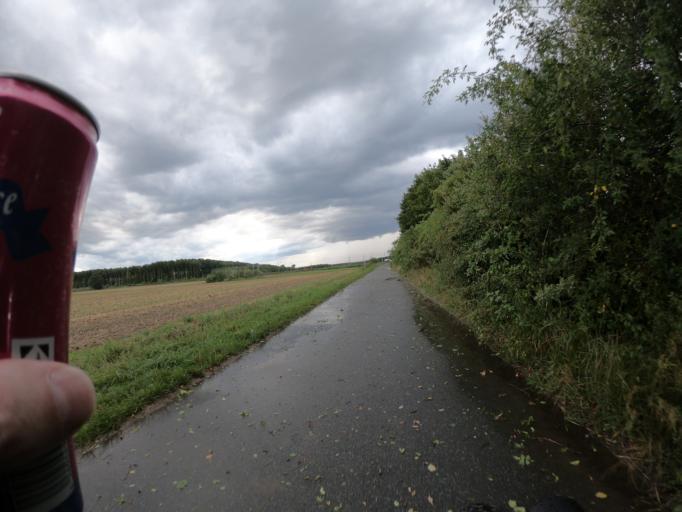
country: DE
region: Hesse
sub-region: Regierungsbezirk Darmstadt
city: Erzhausen
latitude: 49.9596
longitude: 8.6552
